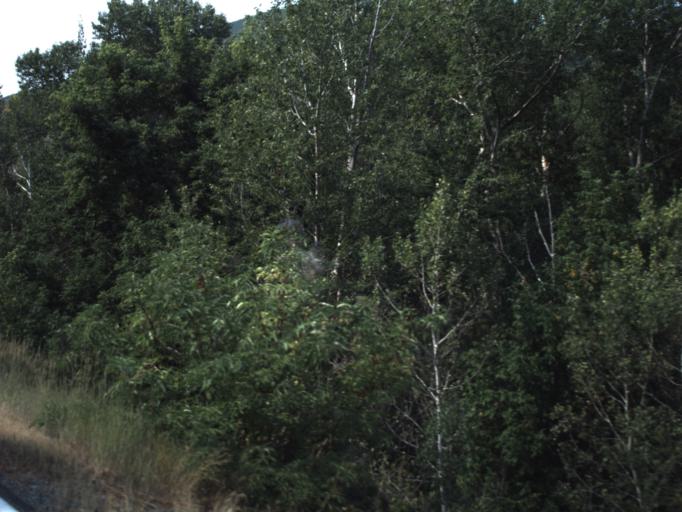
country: US
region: Utah
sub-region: Summit County
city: Summit Park
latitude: 40.8072
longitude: -111.6780
